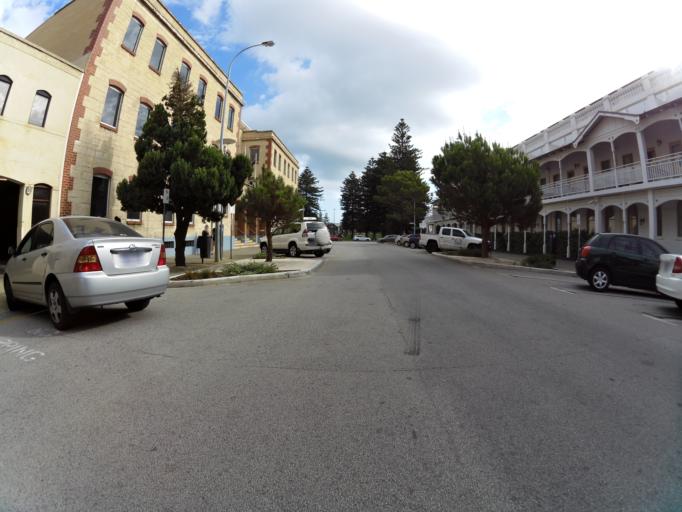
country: AU
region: Western Australia
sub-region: Fremantle
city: South Fremantle
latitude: -32.0574
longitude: 115.7470
